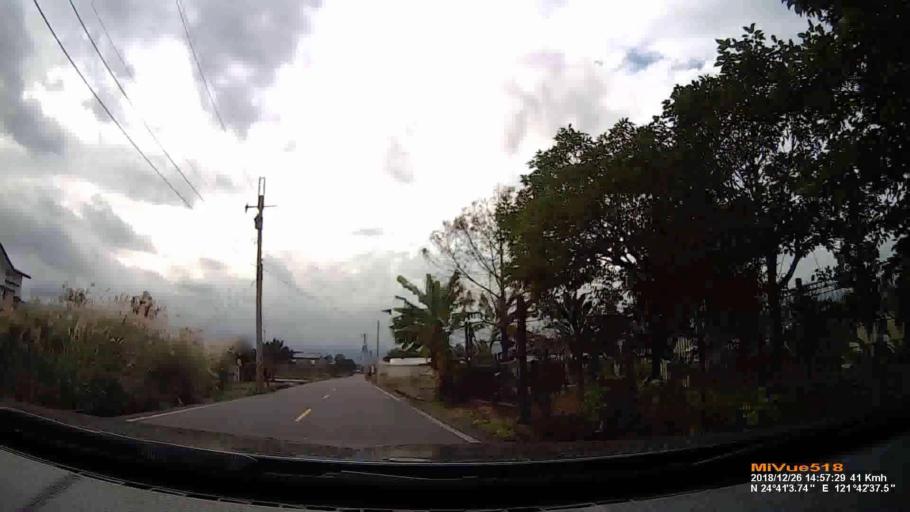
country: TW
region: Taiwan
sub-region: Yilan
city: Yilan
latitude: 24.6844
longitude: 121.7103
